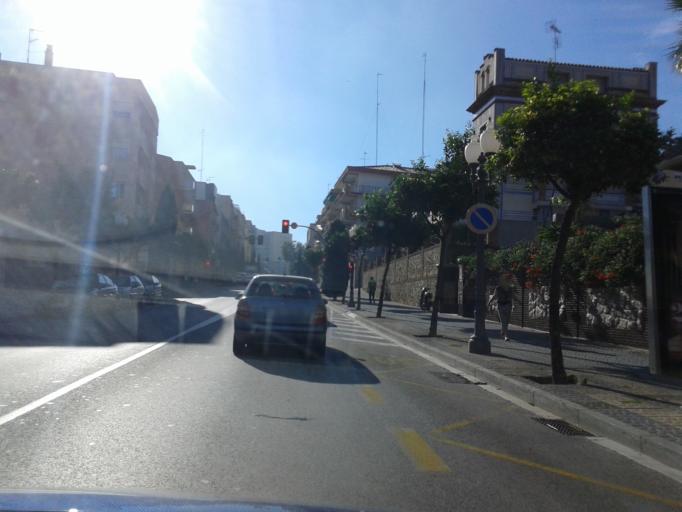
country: ES
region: Catalonia
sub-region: Provincia de Tarragona
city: Tarragona
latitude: 41.1165
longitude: 1.2615
